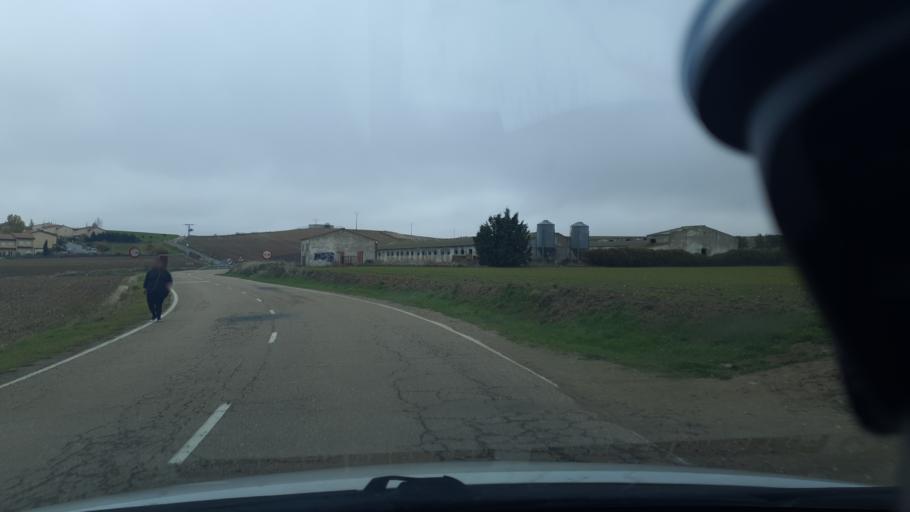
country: ES
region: Castille and Leon
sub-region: Provincia de Segovia
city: Hontanares de Eresma
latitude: 40.9849
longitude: -4.2027
